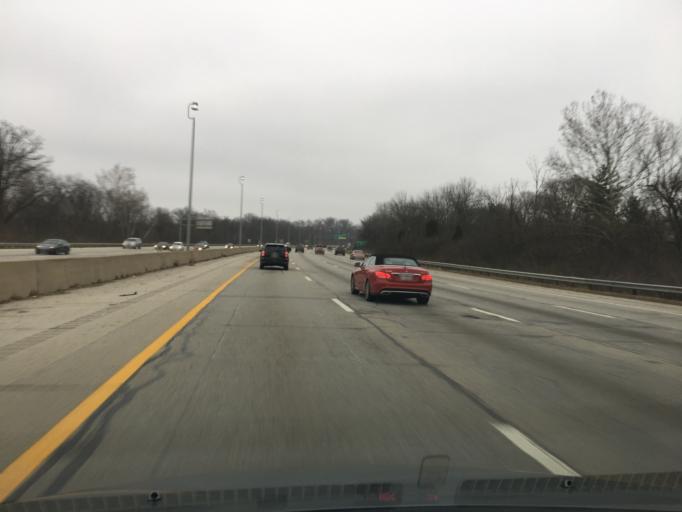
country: US
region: Ohio
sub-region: Hamilton County
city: Highpoint
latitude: 39.2907
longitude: -84.3856
